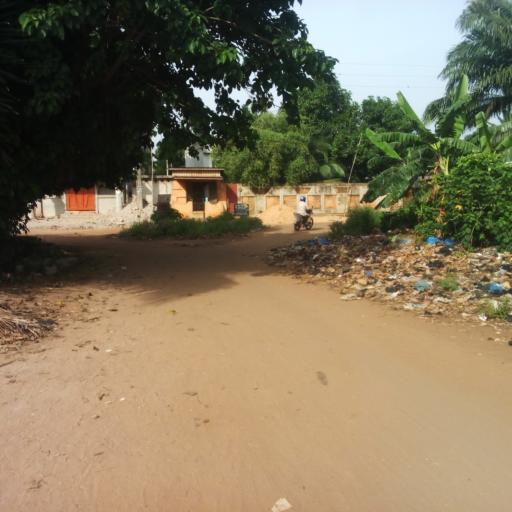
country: BJ
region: Atlantique
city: Abomey-Calavi
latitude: 6.4241
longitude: 2.3338
